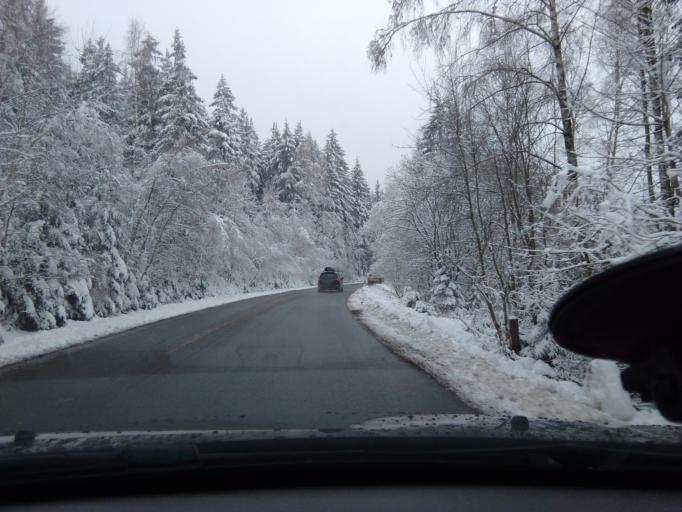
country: DE
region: Saxony
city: Markersbach
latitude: 50.5188
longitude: 12.8609
